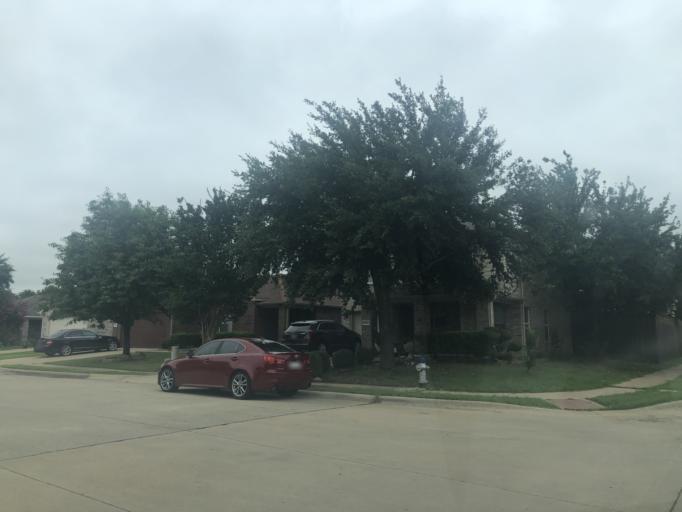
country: US
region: Texas
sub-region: Dallas County
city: Dallas
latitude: 32.7897
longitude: -96.8614
